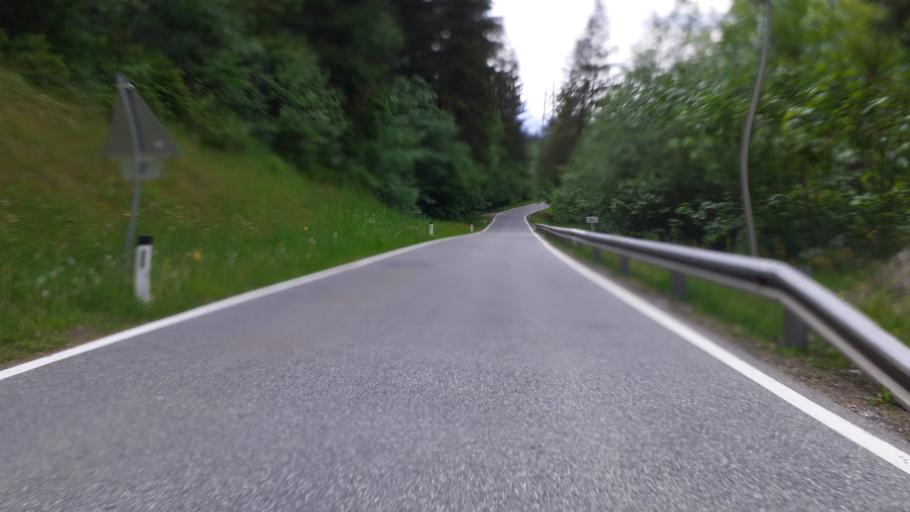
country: AT
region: Vorarlberg
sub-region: Politischer Bezirk Bludenz
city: Innerbraz
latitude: 47.1368
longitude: 9.9359
